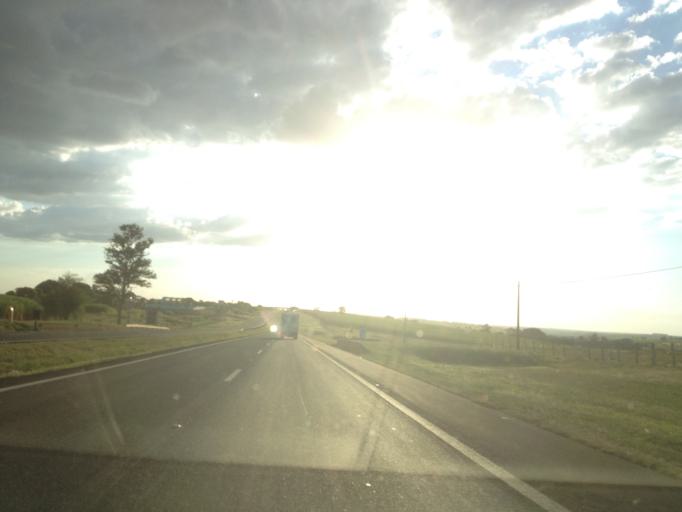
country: BR
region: Sao Paulo
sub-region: Jau
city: Jau
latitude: -22.2706
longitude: -48.4767
